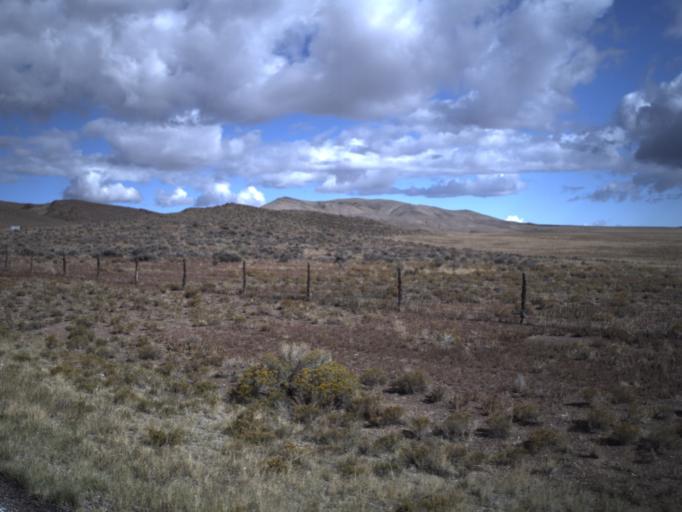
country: US
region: Utah
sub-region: Beaver County
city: Milford
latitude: 38.6013
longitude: -113.8319
